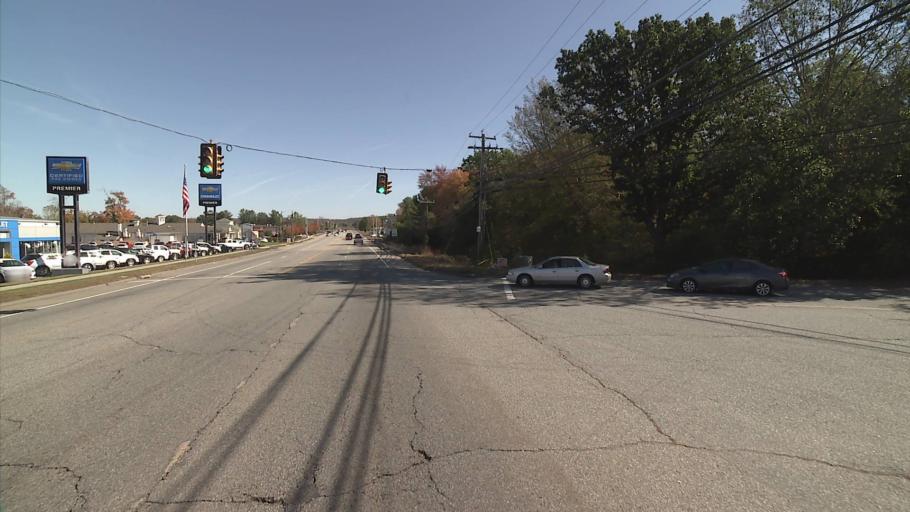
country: US
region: Connecticut
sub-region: Windham County
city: East Brooklyn
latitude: 41.7978
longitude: -71.9069
